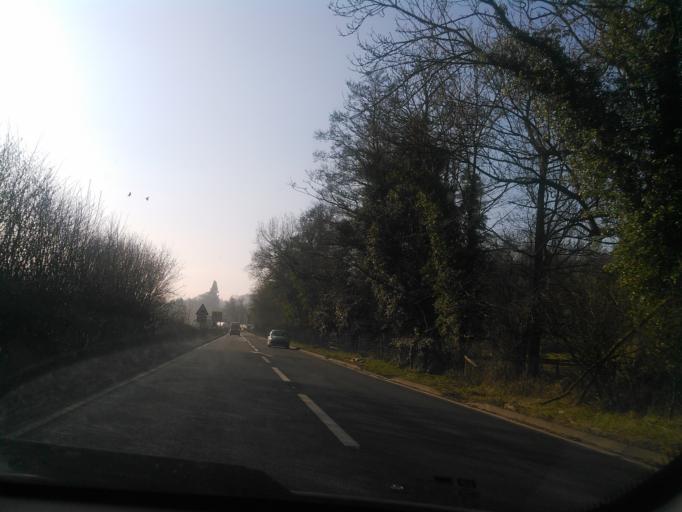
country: GB
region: England
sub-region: Shropshire
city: Church Stretton
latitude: 52.5064
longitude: -2.8240
